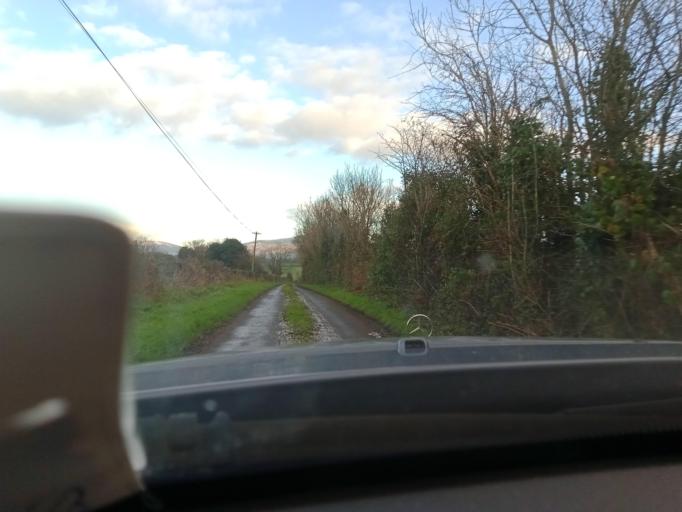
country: IE
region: Leinster
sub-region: Kilkenny
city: Graiguenamanagh
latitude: 52.5180
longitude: -6.9436
